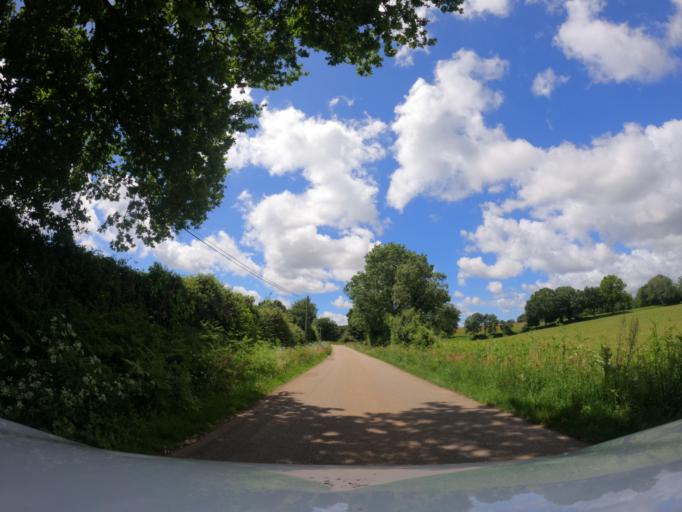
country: FR
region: Pays de la Loire
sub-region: Departement de la Vendee
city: Le Champ-Saint-Pere
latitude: 46.4951
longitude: -1.3547
